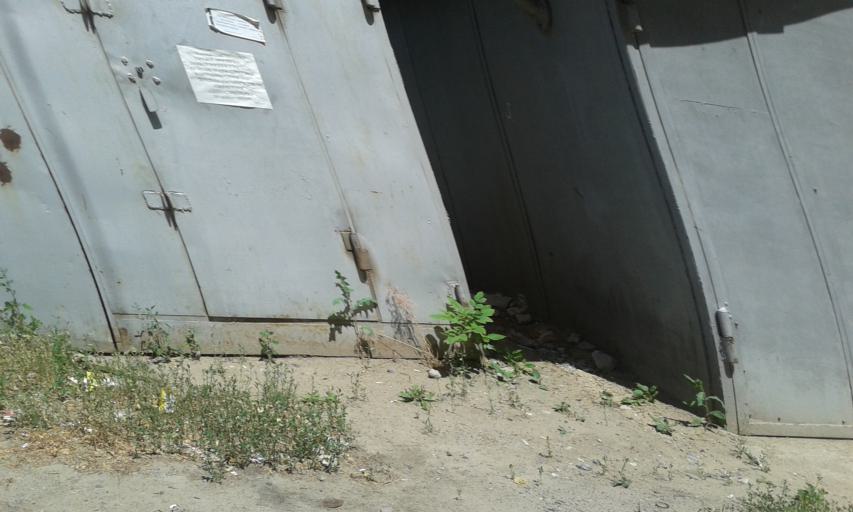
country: RU
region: Volgograd
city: Volgograd
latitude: 48.7546
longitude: 44.5069
